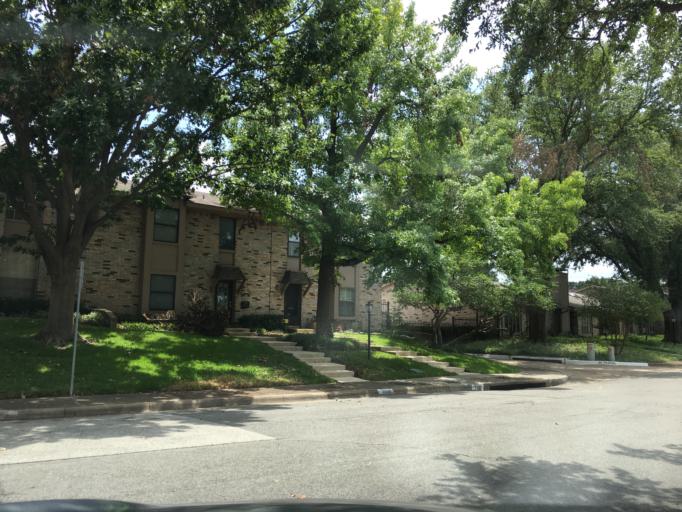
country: US
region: Texas
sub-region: Dallas County
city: University Park
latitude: 32.8920
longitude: -96.7760
